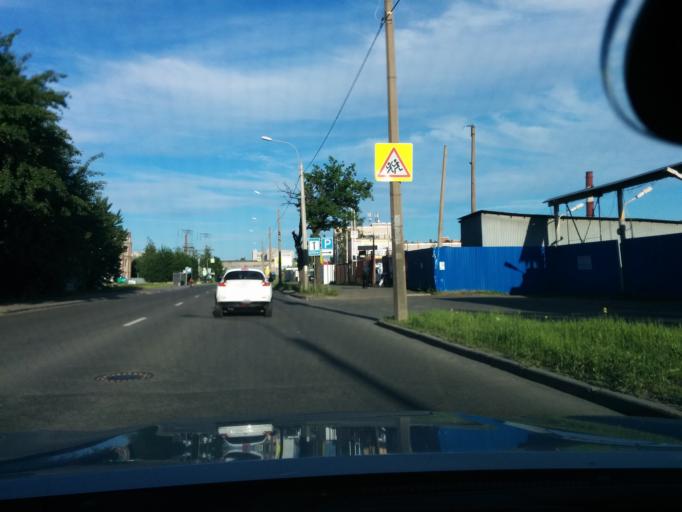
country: RU
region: Leningrad
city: Finlyandskiy
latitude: 59.9758
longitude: 30.3720
